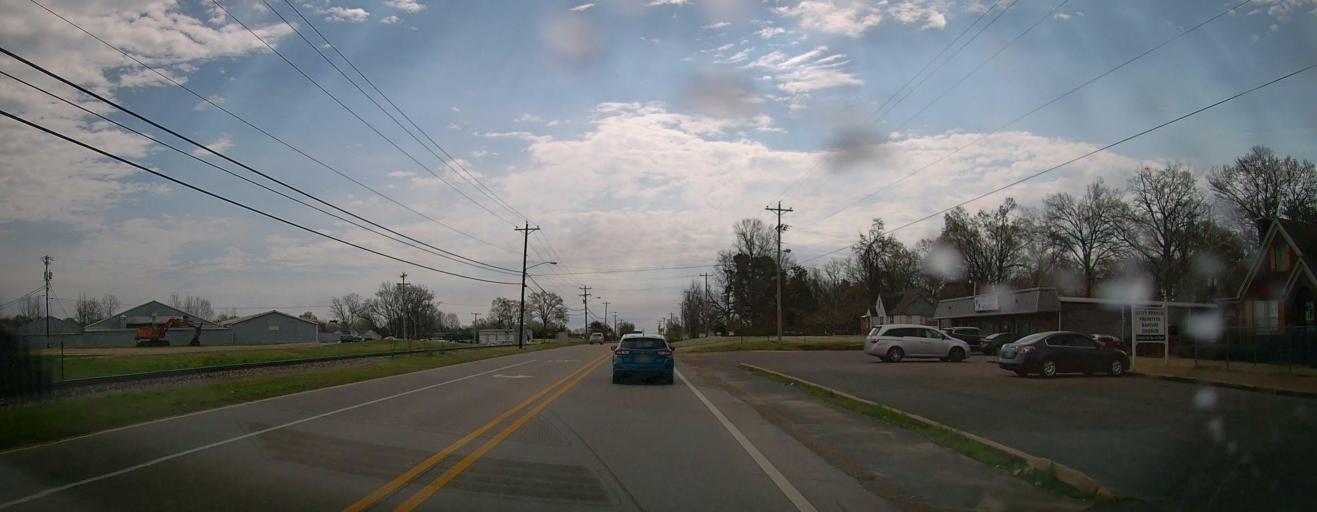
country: US
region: Mississippi
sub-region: De Soto County
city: Olive Branch
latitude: 34.9597
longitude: -89.8218
